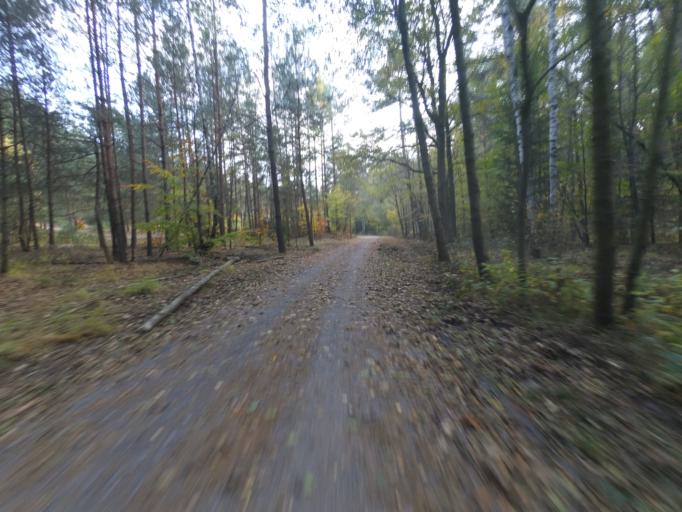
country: DE
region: Saxony
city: Albertstadt
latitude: 51.0977
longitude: 13.8268
